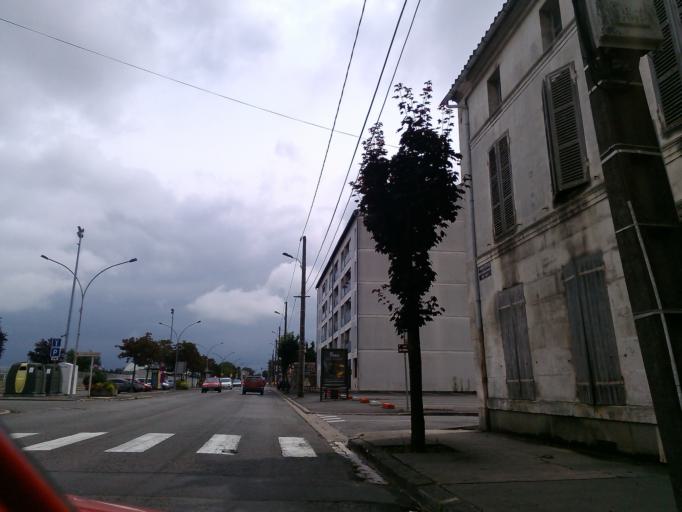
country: FR
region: Poitou-Charentes
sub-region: Departement de la Charente
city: Cognac
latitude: 45.6887
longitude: -0.3154
